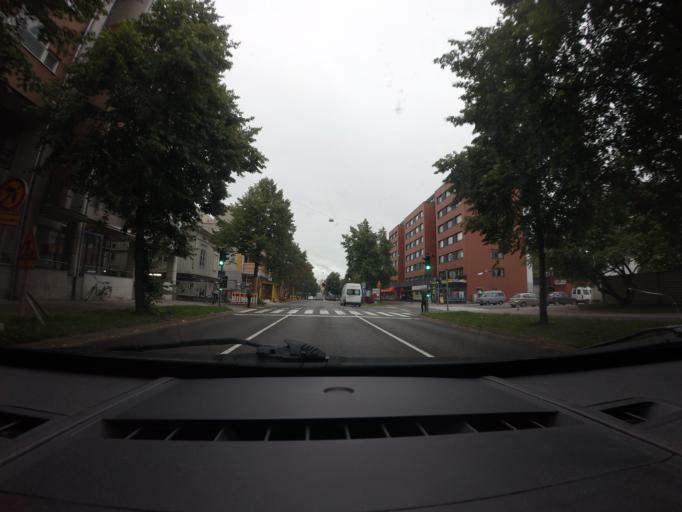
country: FI
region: Varsinais-Suomi
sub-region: Turku
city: Turku
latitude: 60.4478
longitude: 22.2510
